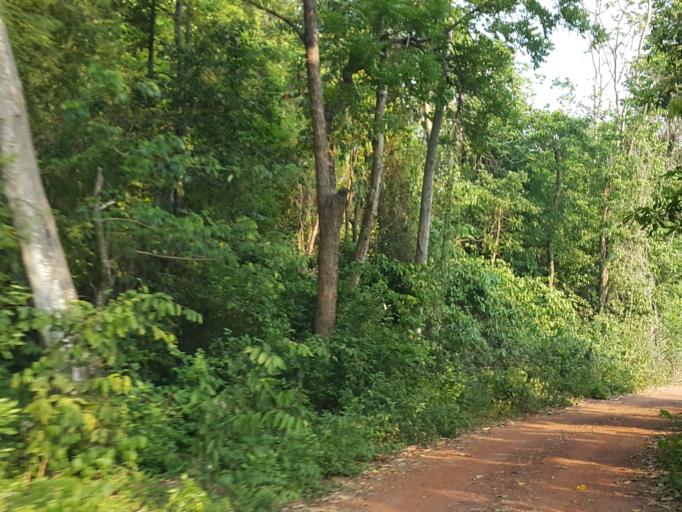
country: TH
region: Uthai Thani
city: Huai Khot
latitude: 15.3270
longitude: 99.6768
